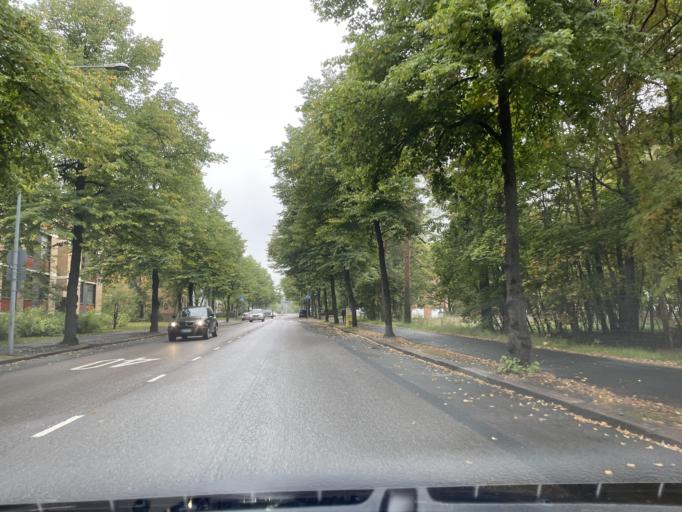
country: FI
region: Uusimaa
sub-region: Helsinki
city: Hyvinge
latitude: 60.6230
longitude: 24.8492
